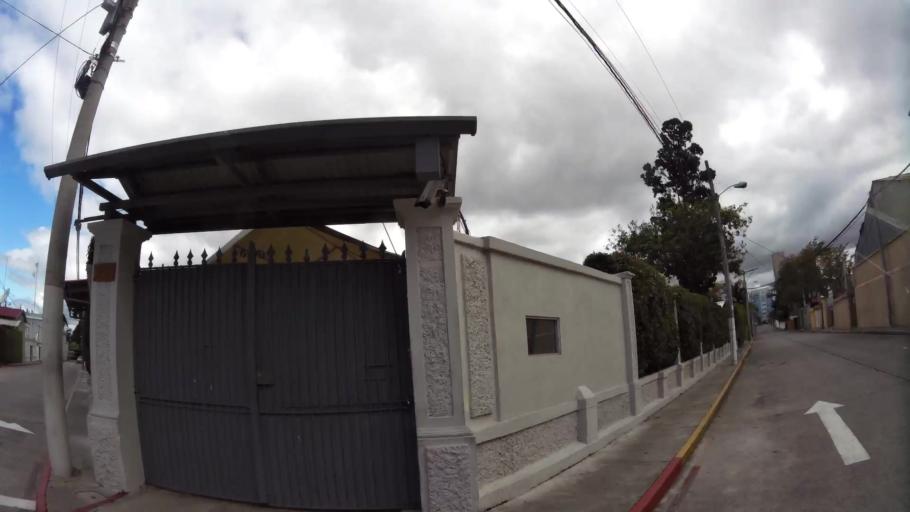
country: GT
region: Guatemala
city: Guatemala City
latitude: 14.6107
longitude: -90.5138
